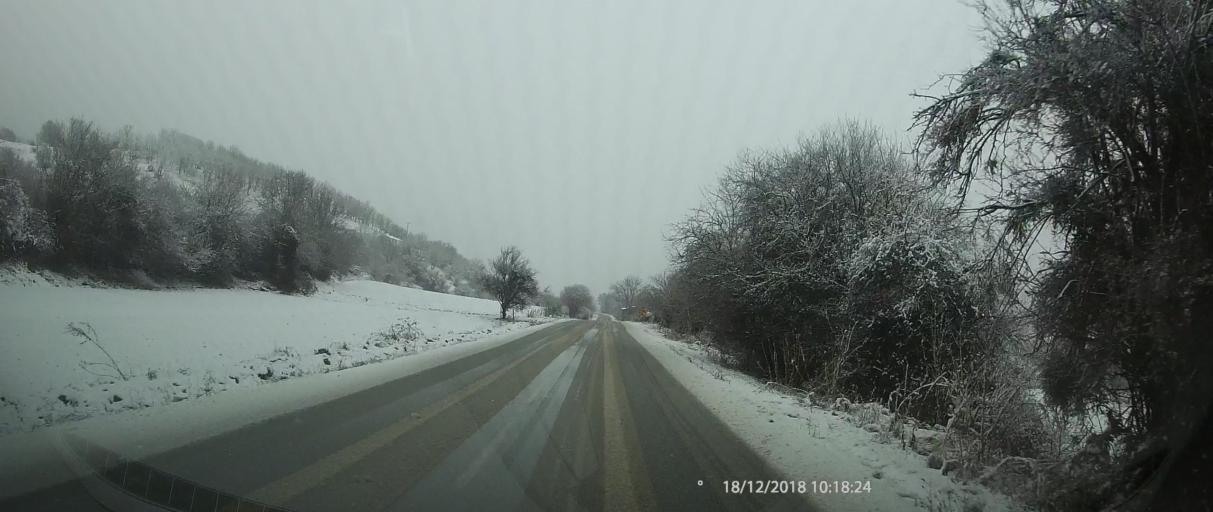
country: GR
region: Thessaly
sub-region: Nomos Larisis
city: Livadi
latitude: 40.1314
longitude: 22.2169
